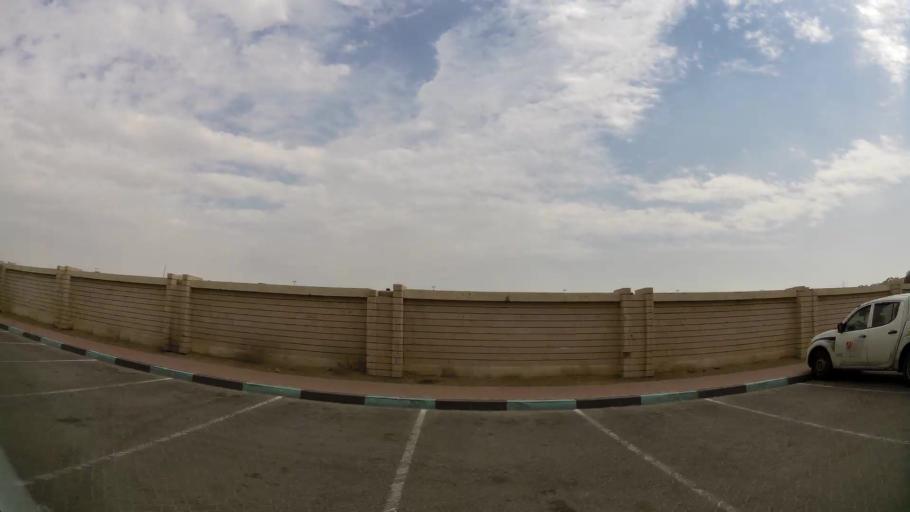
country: OM
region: Al Buraimi
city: Al Buraymi
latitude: 24.2222
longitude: 55.7835
